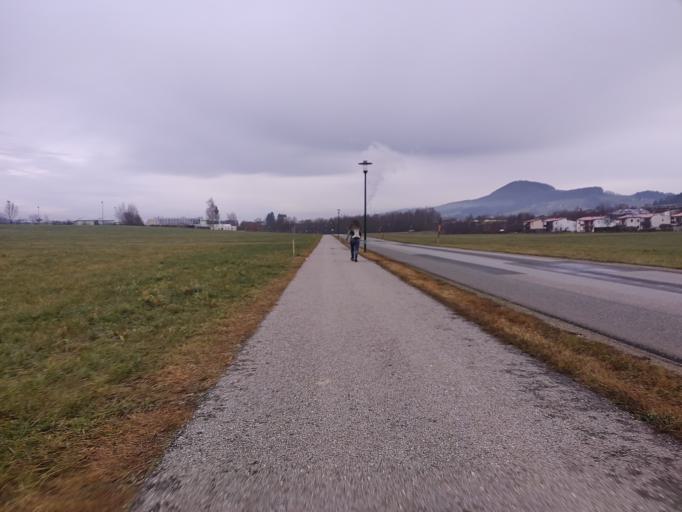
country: AT
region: Salzburg
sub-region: Politischer Bezirk Salzburg-Umgebung
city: Obertrum am See
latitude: 47.9299
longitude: 13.0751
